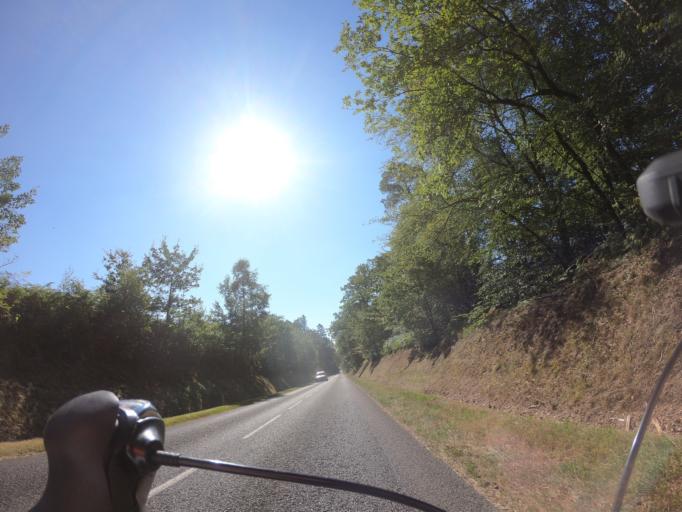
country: FR
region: Lower Normandy
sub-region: Departement de l'Orne
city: Tesse-la-Madeleine
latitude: 48.5722
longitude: -0.4525
